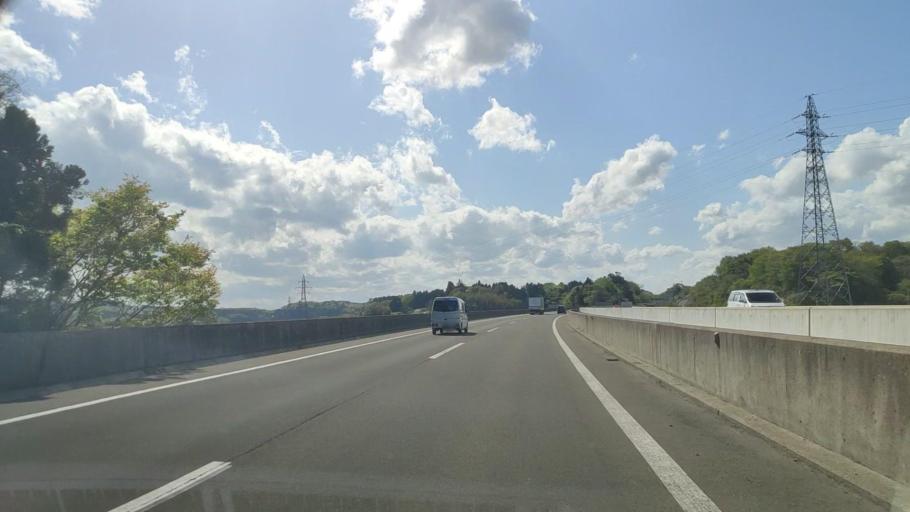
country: JP
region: Miyagi
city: Matsushima
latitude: 38.4101
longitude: 141.1270
